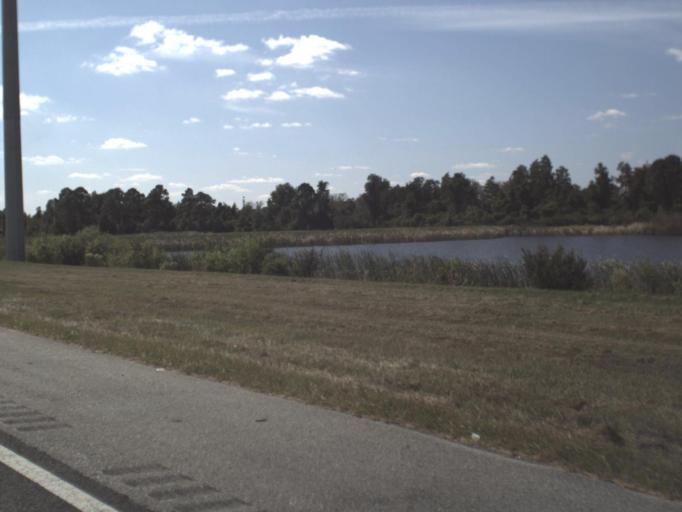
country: US
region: Florida
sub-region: Polk County
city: Citrus Ridge
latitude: 28.3525
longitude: -81.6146
